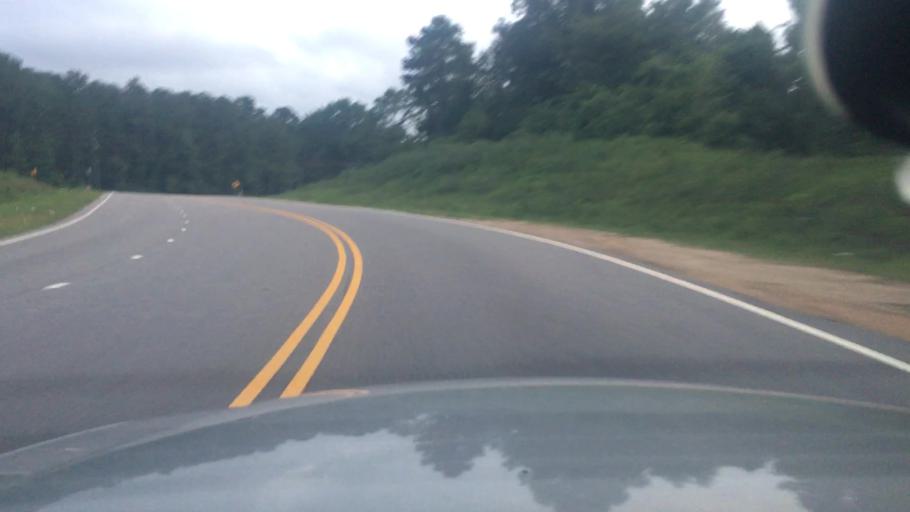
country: US
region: North Carolina
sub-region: Cumberland County
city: Hope Mills
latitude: 34.9695
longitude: -78.9162
